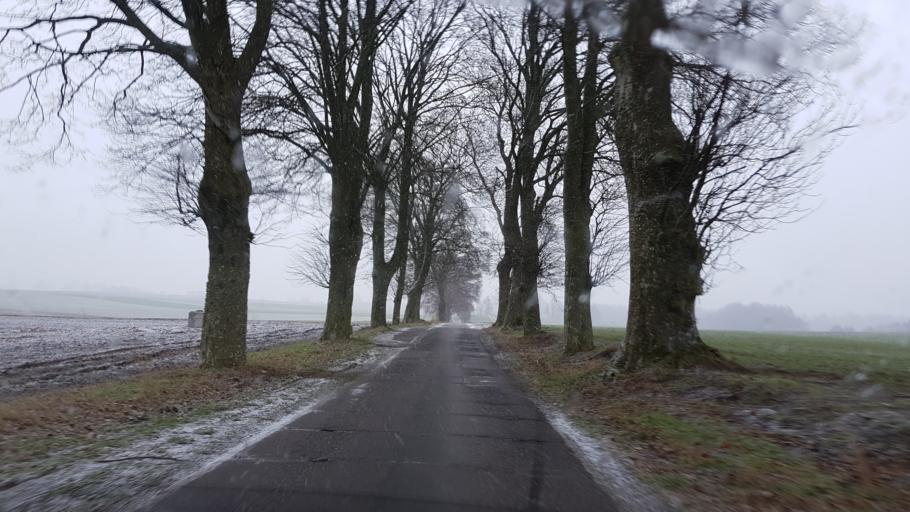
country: PL
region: West Pomeranian Voivodeship
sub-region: Powiat slawienski
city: Slawno
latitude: 54.2787
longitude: 16.6157
